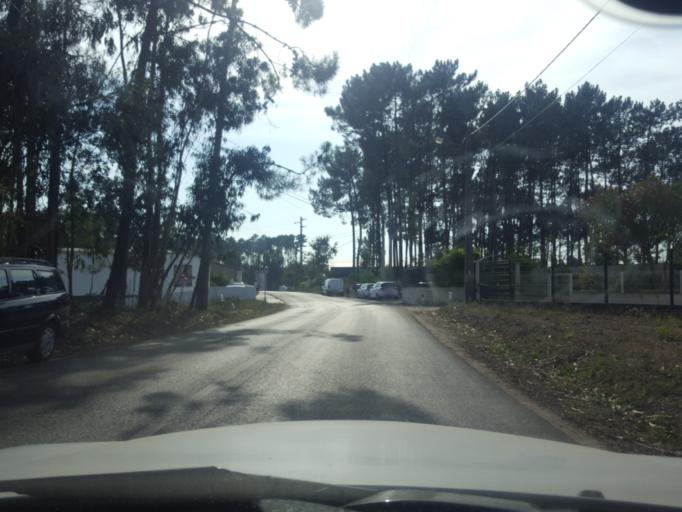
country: PT
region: Leiria
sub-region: Leiria
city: Leiria
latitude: 39.7260
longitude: -8.7694
